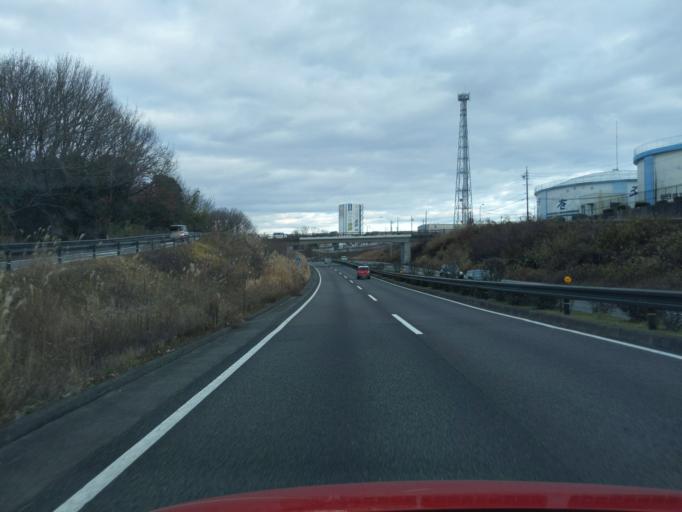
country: JP
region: Aichi
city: Kasugai
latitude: 35.2798
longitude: 137.0142
